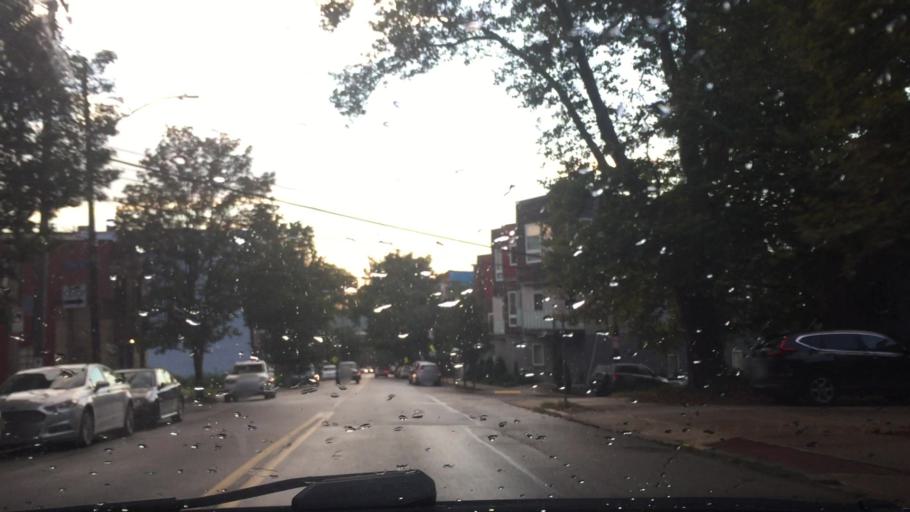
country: US
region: Pennsylvania
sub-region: Allegheny County
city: Bloomfield
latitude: 40.4645
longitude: -79.9622
